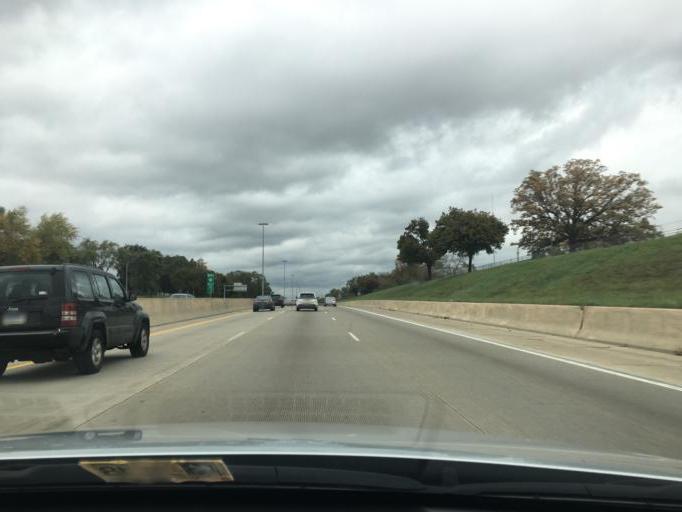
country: US
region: Michigan
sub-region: Oakland County
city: Southfield
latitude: 42.4454
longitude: -83.2197
